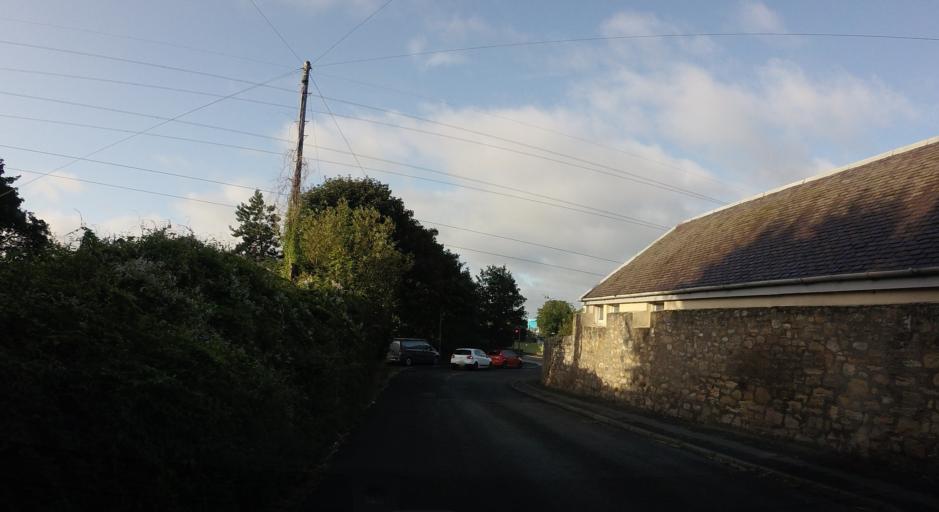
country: GB
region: Scotland
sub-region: East Lothian
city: Musselburgh
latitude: 55.9095
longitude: -3.0123
